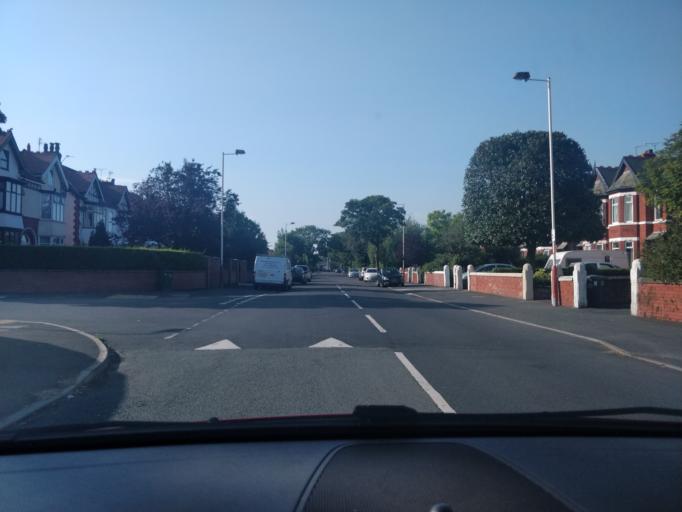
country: GB
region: England
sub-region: Sefton
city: Southport
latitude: 53.6508
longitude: -2.9738
